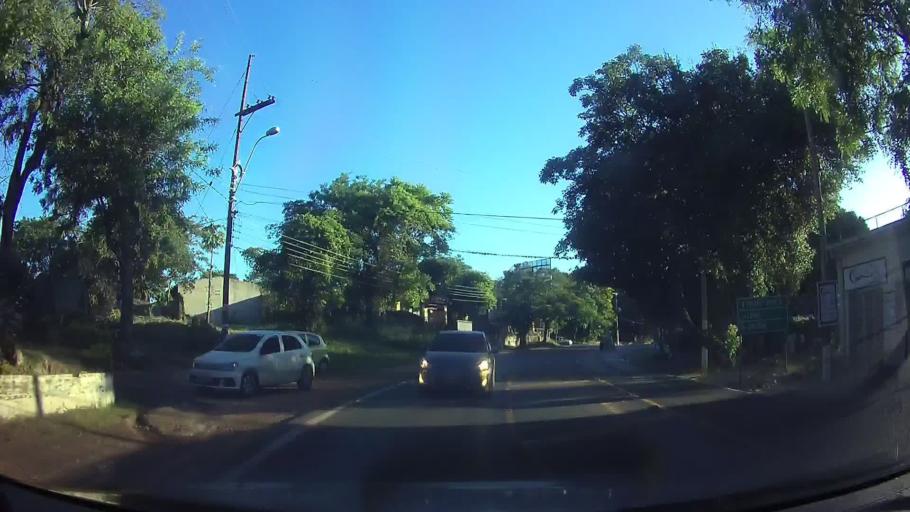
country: PY
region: Central
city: Aregua
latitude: -25.3192
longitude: -57.3883
